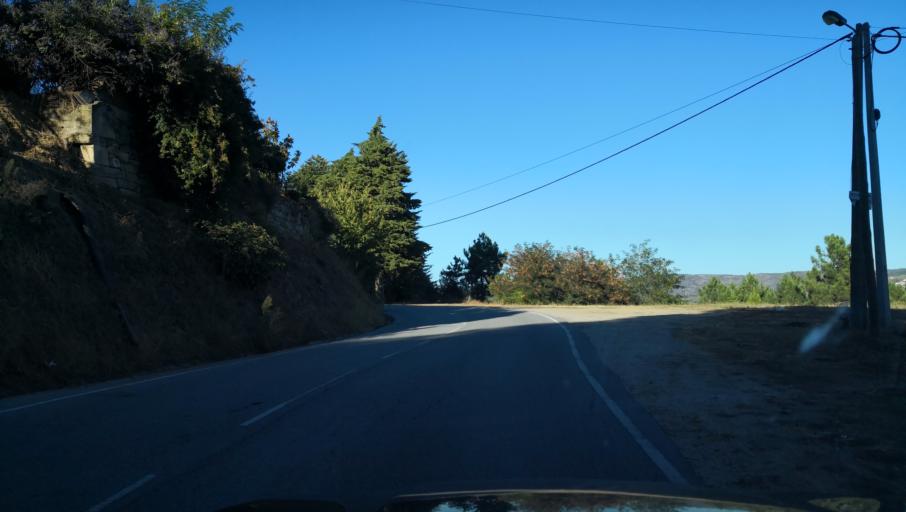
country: PT
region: Vila Real
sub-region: Sabrosa
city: Sabrosa
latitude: 41.2722
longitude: -7.5686
